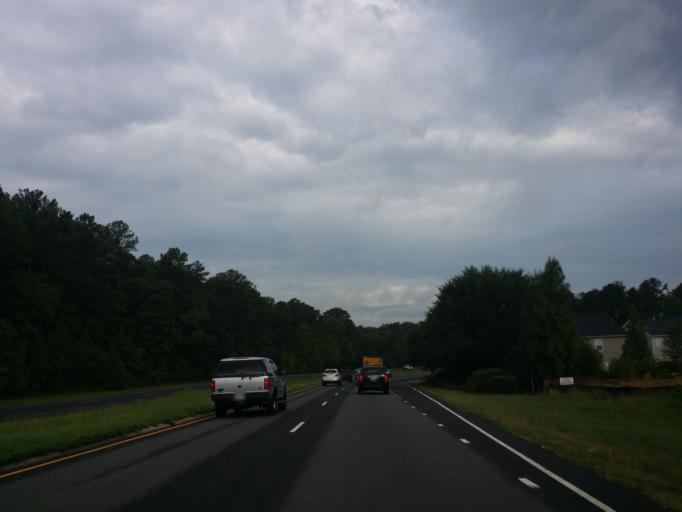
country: US
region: North Carolina
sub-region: Wake County
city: Morrisville
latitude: 35.9199
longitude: -78.8287
